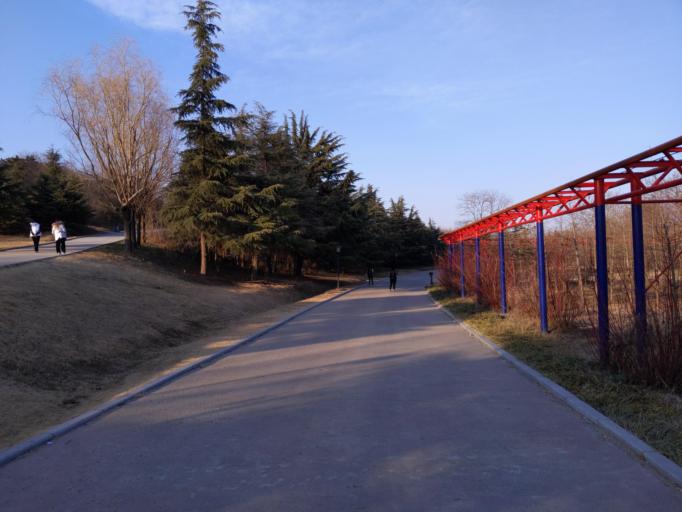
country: CN
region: Henan Sheng
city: Puyang
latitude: 35.7785
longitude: 114.9505
